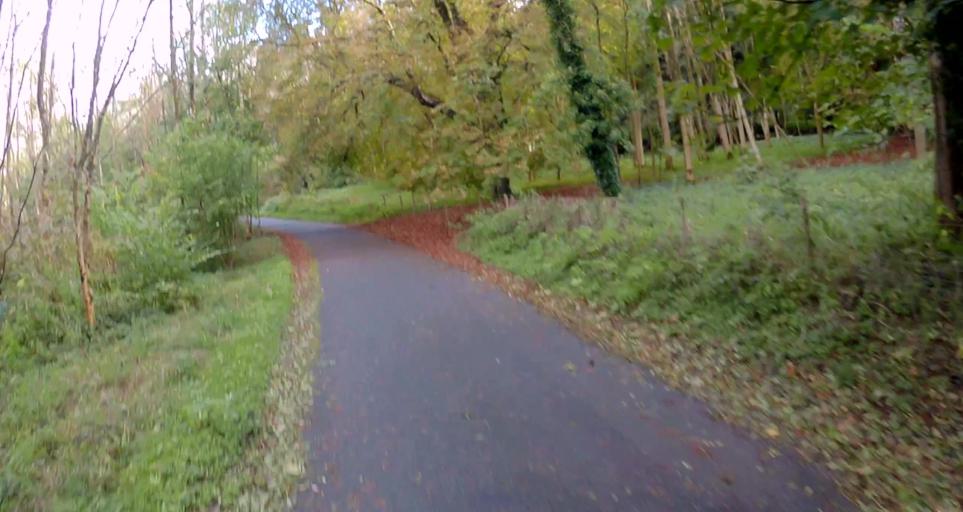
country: GB
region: England
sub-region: Hampshire
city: Kings Worthy
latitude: 51.0864
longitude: -1.2546
